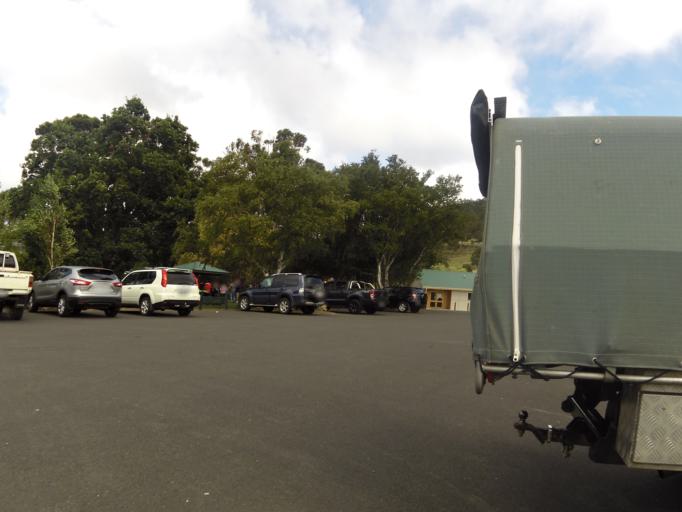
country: AU
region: Tasmania
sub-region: Huon Valley
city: Franklin
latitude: -42.9979
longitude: 146.9282
